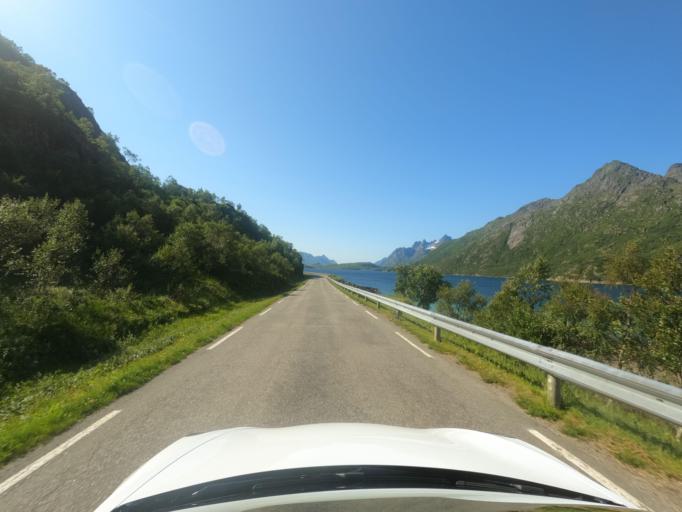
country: NO
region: Nordland
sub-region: Hadsel
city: Stokmarknes
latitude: 68.3856
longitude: 15.0917
